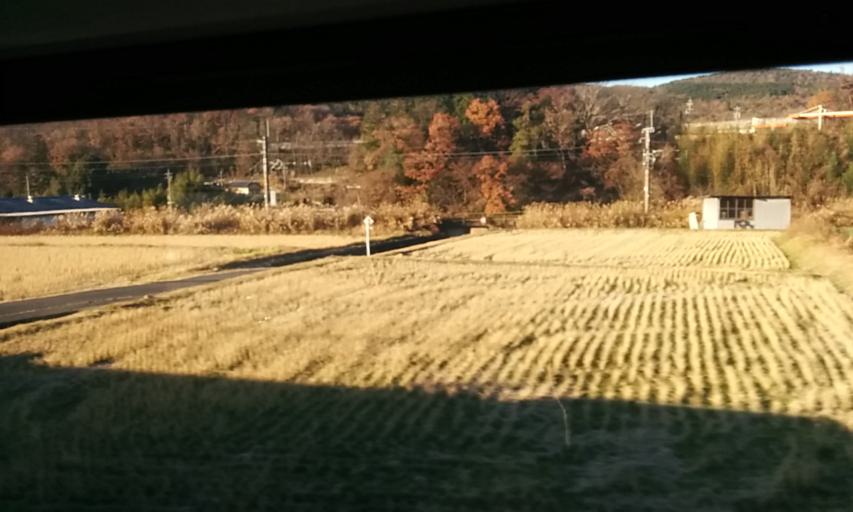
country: JP
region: Gifu
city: Mizunami
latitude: 35.4389
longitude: 137.3615
